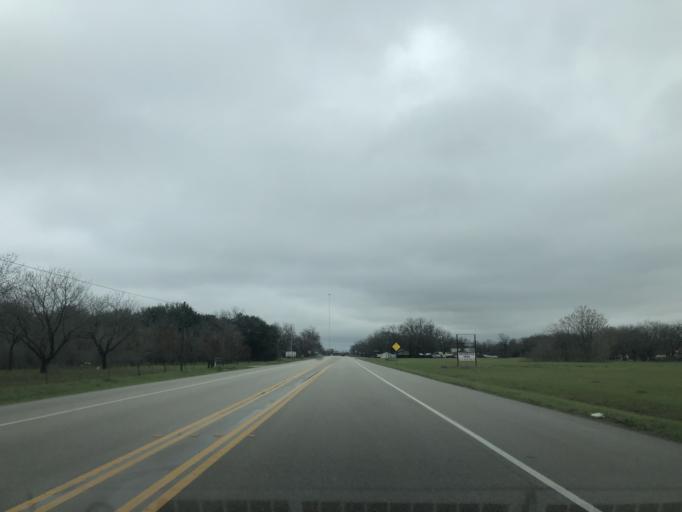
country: US
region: Texas
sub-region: Williamson County
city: Hutto
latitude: 30.6397
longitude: -97.5464
